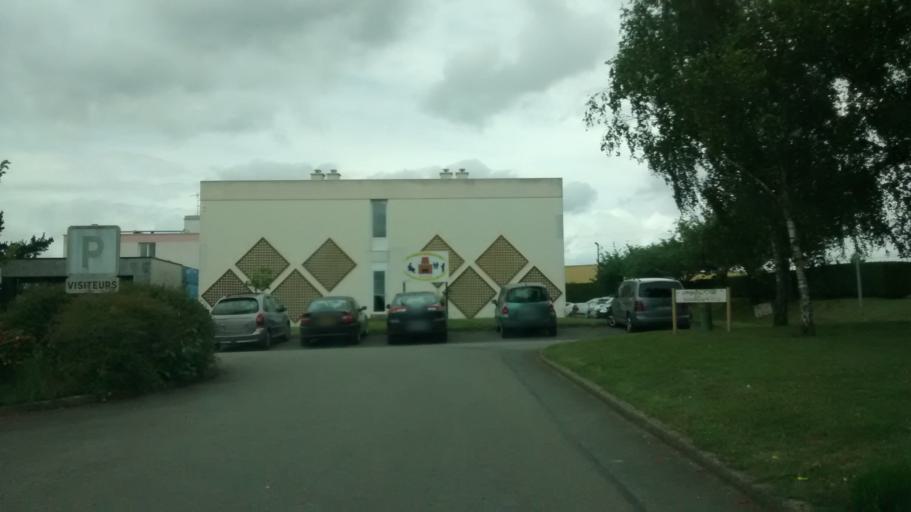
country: FR
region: Brittany
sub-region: Departement du Morbihan
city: Carentoir
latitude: 47.8186
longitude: -2.1329
